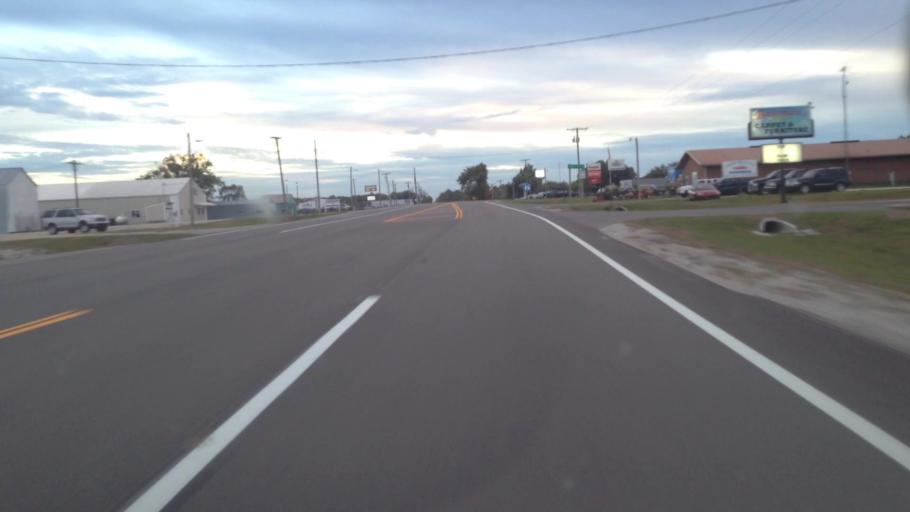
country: US
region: Kansas
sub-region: Anderson County
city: Garnett
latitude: 38.2931
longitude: -95.2492
